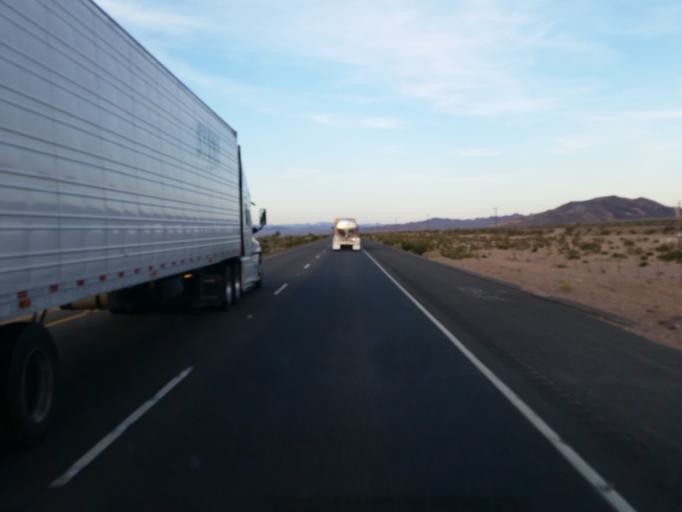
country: US
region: California
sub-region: San Bernardino County
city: Joshua Tree
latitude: 34.7287
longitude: -116.2635
